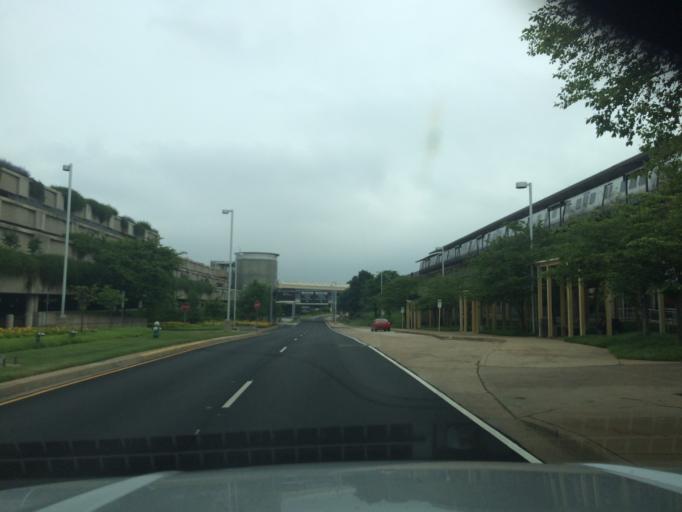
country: US
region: Washington, D.C.
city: Washington, D.C.
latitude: 38.8531
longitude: -77.0442
